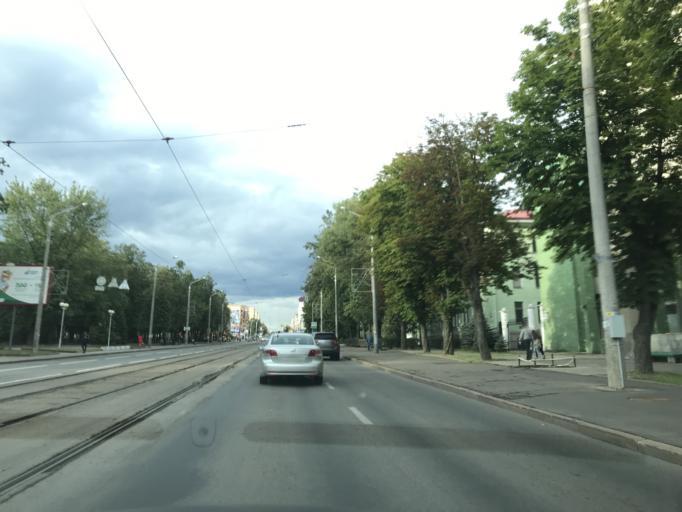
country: BY
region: Minsk
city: Minsk
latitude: 53.9234
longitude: 27.5913
